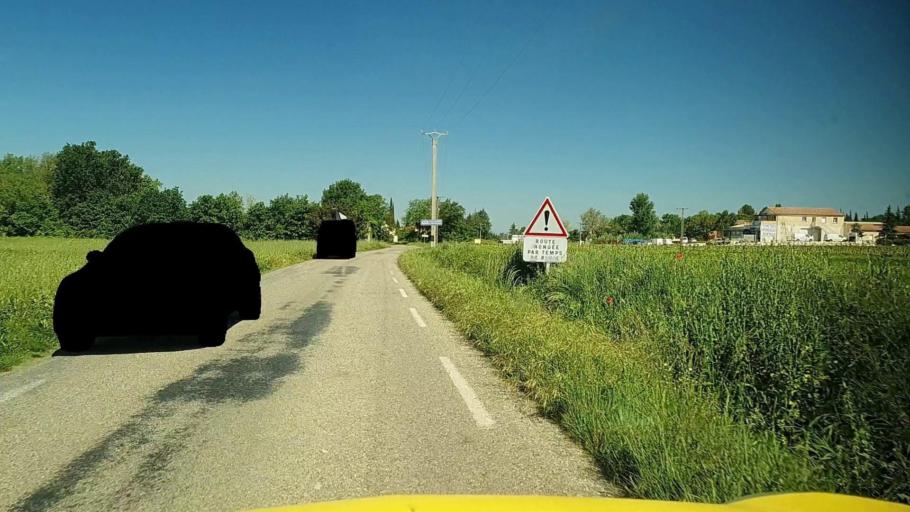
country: FR
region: Languedoc-Roussillon
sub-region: Departement du Gard
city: Moussac
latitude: 43.9912
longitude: 4.2207
